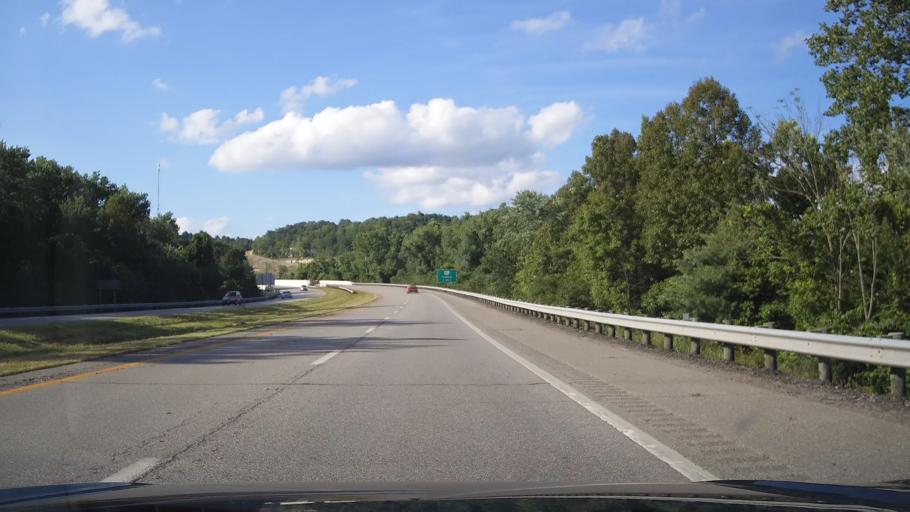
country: US
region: Ohio
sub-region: Lawrence County
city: Coal Grove
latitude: 38.5109
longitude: -82.6523
